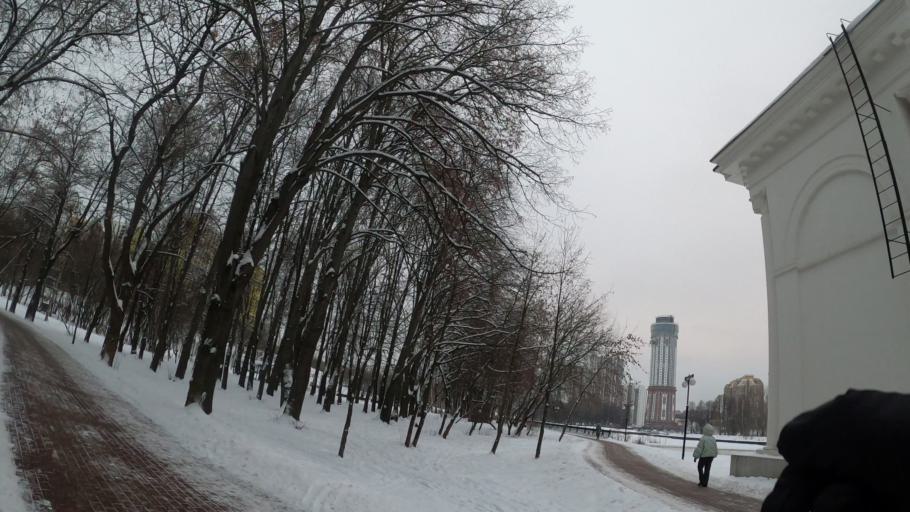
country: RU
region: Moskovskaya
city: Levoberezhnaya
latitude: 55.9022
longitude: 37.4709
